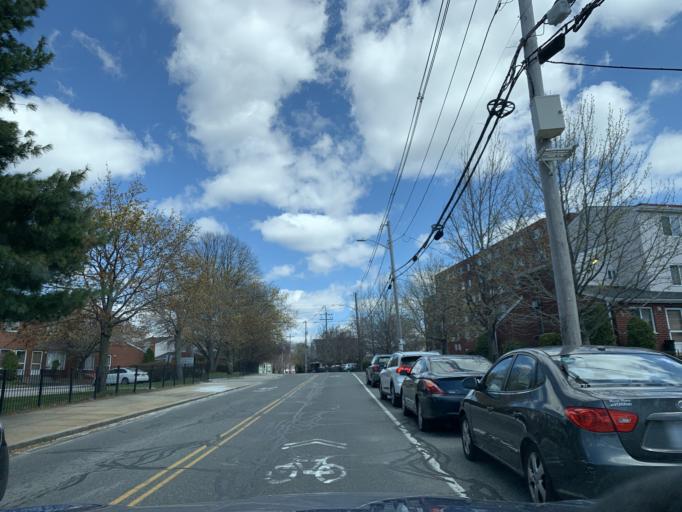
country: US
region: Rhode Island
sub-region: Providence County
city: Providence
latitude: 41.8119
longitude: -71.4152
